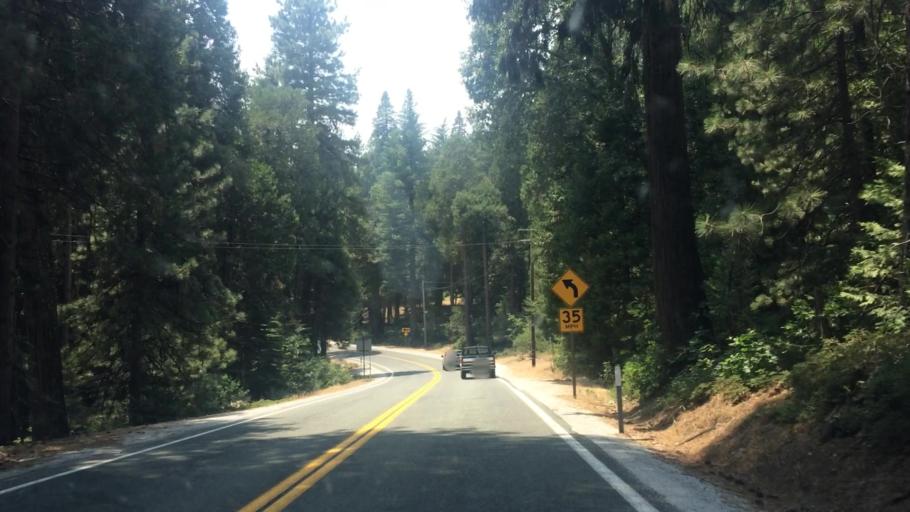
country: US
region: California
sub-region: Amador County
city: Pioneer
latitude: 38.5104
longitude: -120.4890
